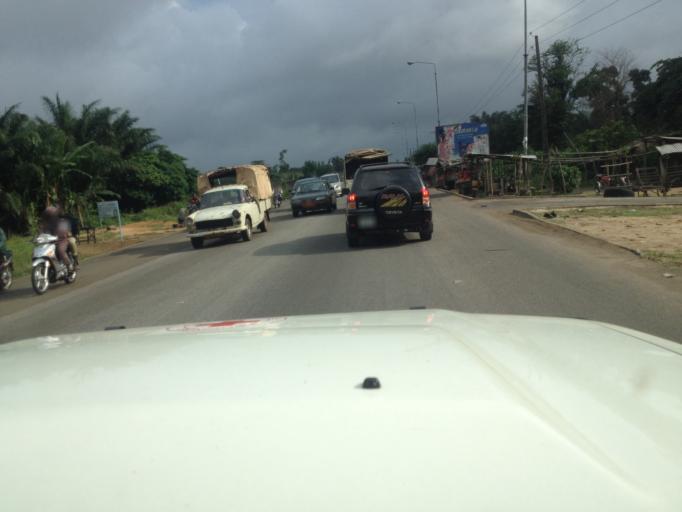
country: BJ
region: Queme
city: Porto-Novo
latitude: 6.4421
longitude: 2.6224
